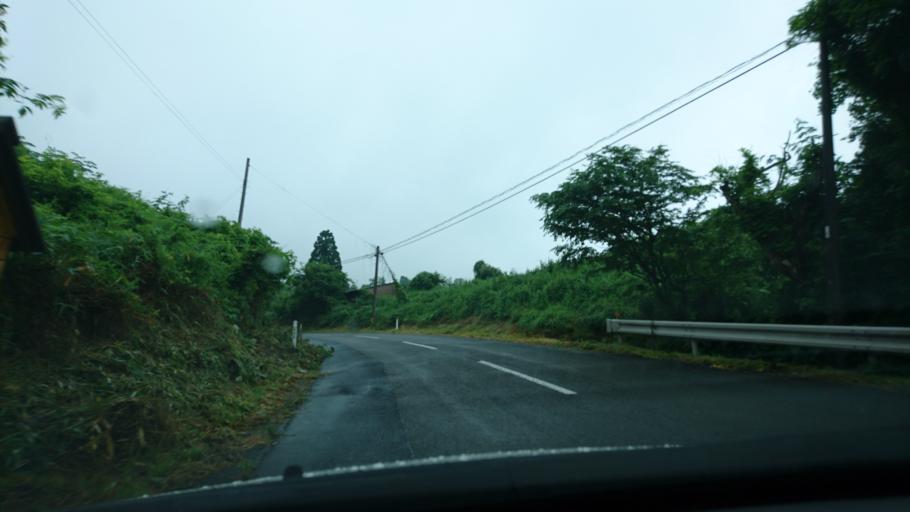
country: JP
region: Iwate
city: Ichinoseki
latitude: 38.9092
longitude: 141.0317
